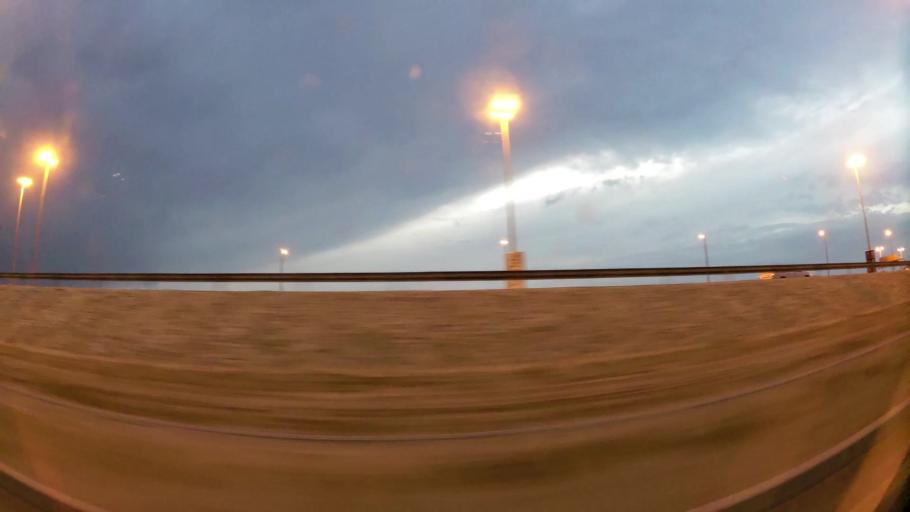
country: BH
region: Central Governorate
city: Madinat Hamad
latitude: 26.1434
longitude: 50.5106
